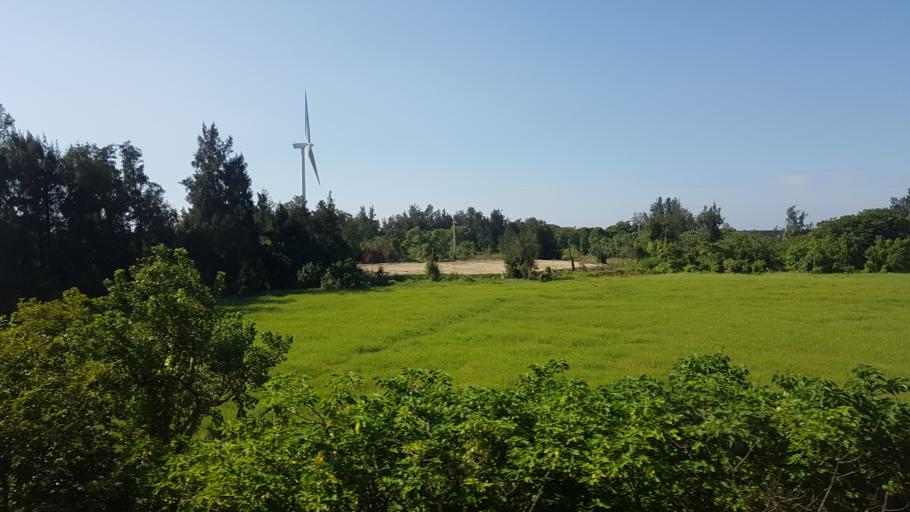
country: TW
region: Taiwan
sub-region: Hsinchu
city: Hsinchu
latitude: 24.7433
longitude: 120.9033
